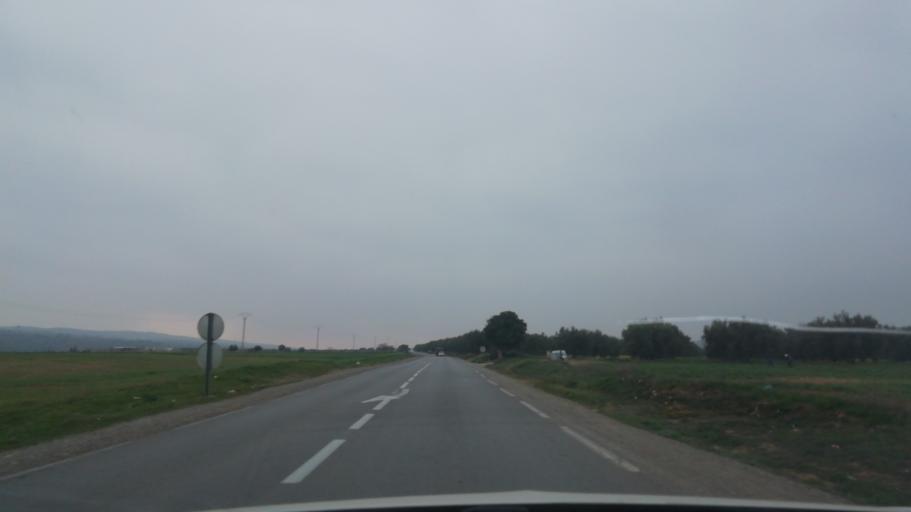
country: DZ
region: Sidi Bel Abbes
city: Sfizef
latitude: 35.2707
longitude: -0.1582
